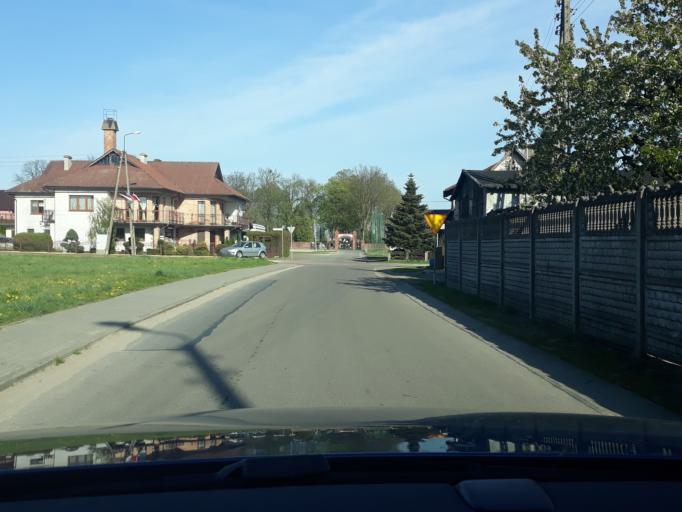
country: PL
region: Pomeranian Voivodeship
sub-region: Powiat czluchowski
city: Przechlewo
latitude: 53.8242
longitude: 17.3797
